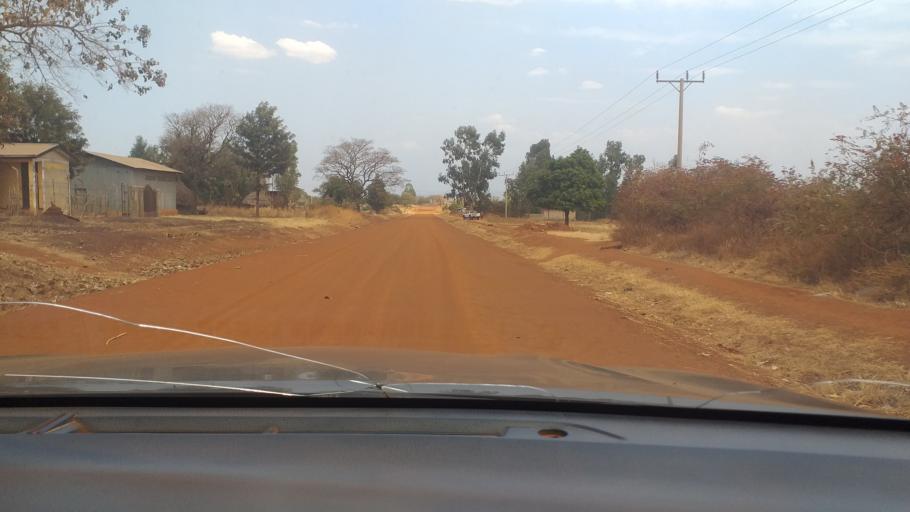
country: ET
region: Binshangul Gumuz
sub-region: Asosa
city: Asosa
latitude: 10.0623
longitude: 34.6945
